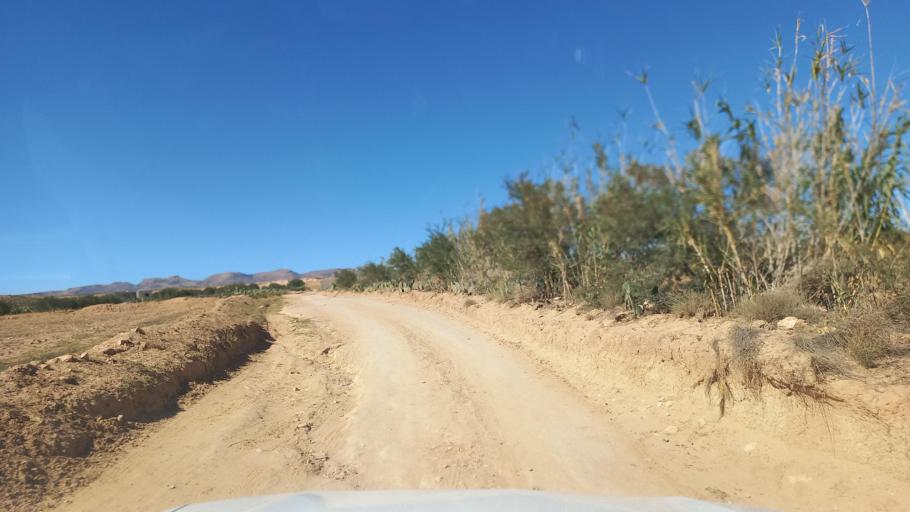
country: TN
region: Al Qasrayn
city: Sbiba
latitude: 35.3749
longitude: 9.0925
